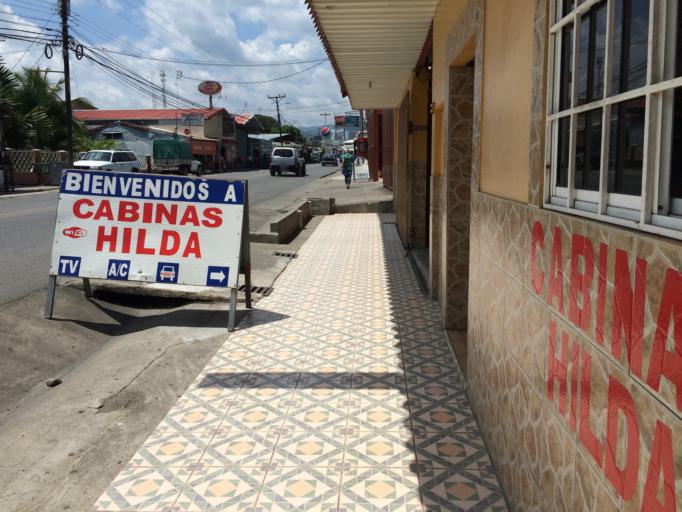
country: CR
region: Puntarenas
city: Canoas
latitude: 8.5327
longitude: -82.8394
